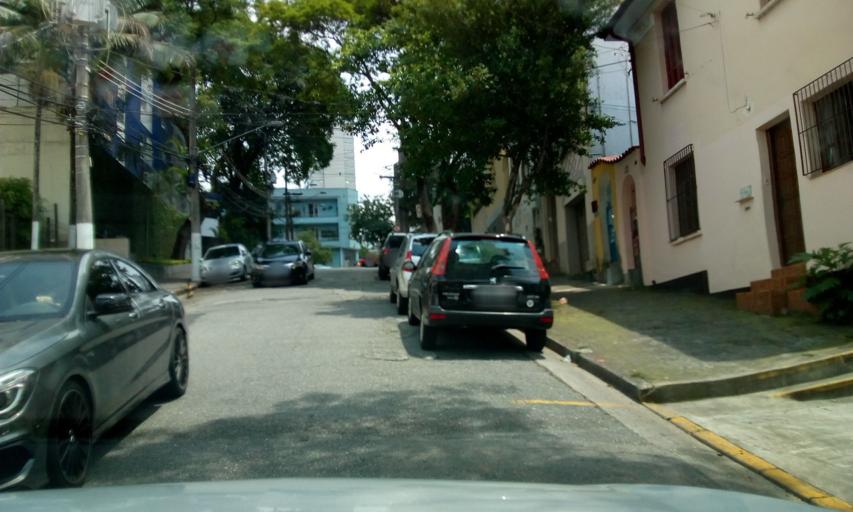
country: BR
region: Sao Paulo
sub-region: Sao Paulo
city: Sao Paulo
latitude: -23.5729
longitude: -46.6366
